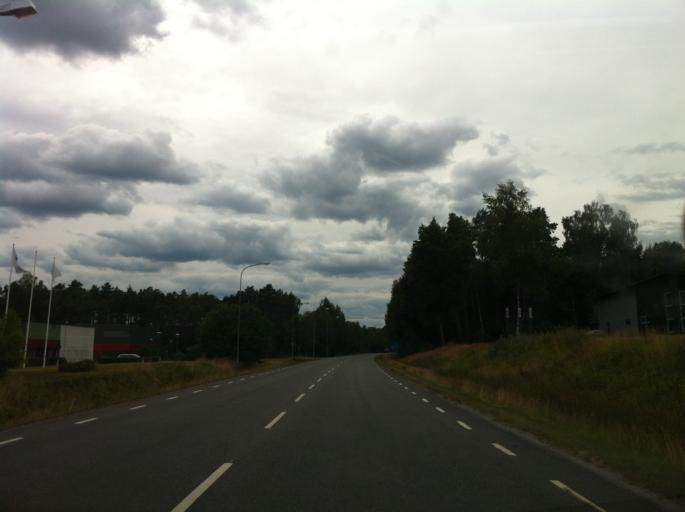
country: SE
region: Skane
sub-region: Osby Kommun
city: Lonsboda
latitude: 56.3933
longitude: 14.3085
